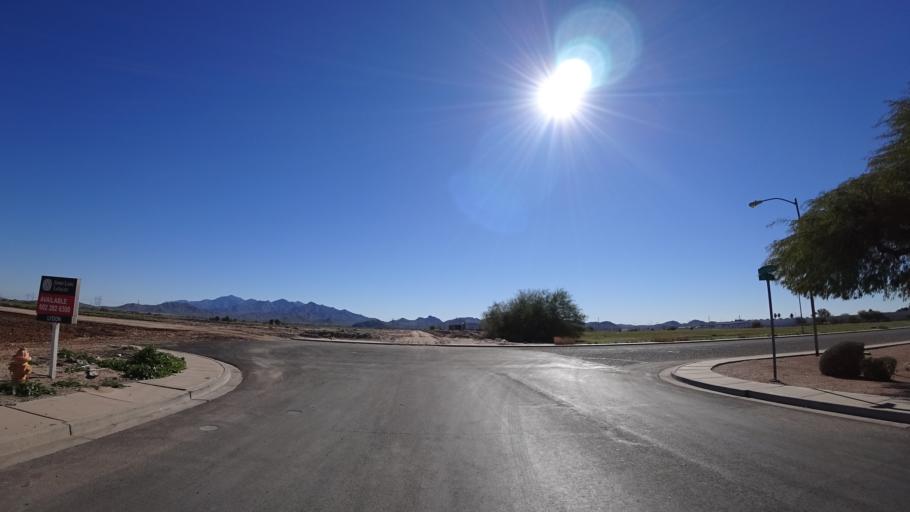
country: US
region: Arizona
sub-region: Maricopa County
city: Goodyear
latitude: 33.4138
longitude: -112.3713
